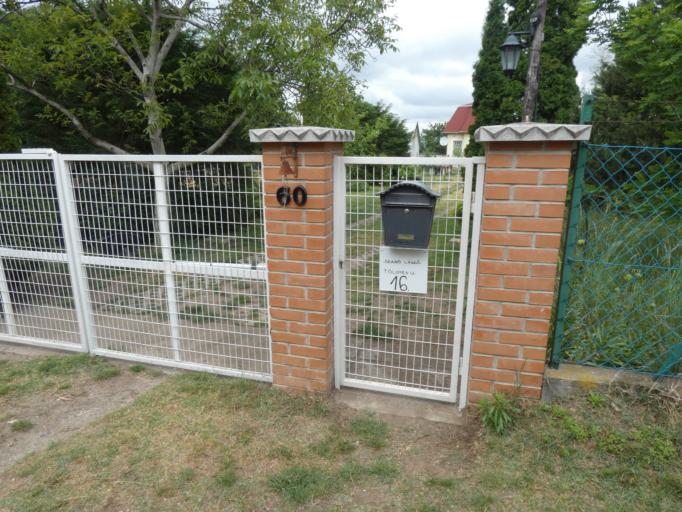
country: HU
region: Pest
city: Kerepes
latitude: 47.5959
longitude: 19.2860
